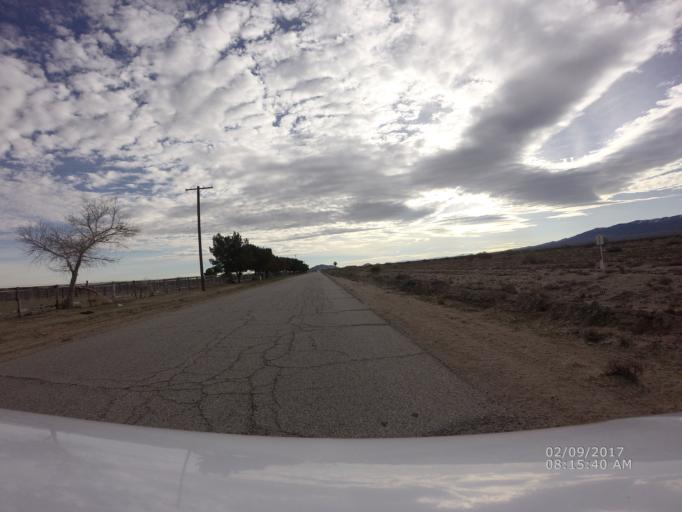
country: US
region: California
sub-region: Los Angeles County
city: Lake Los Angeles
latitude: 34.5580
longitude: -117.8294
